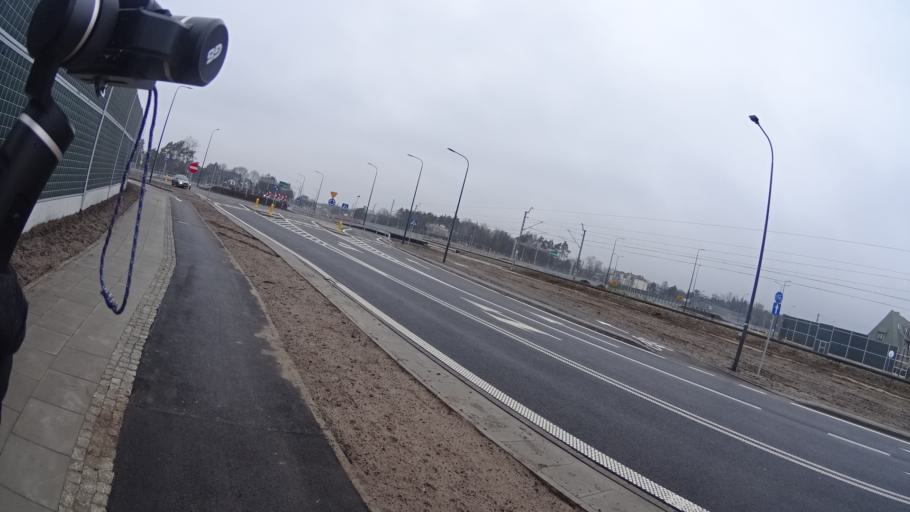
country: PL
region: Masovian Voivodeship
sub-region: Warszawa
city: Wawer
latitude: 52.1676
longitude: 21.2048
